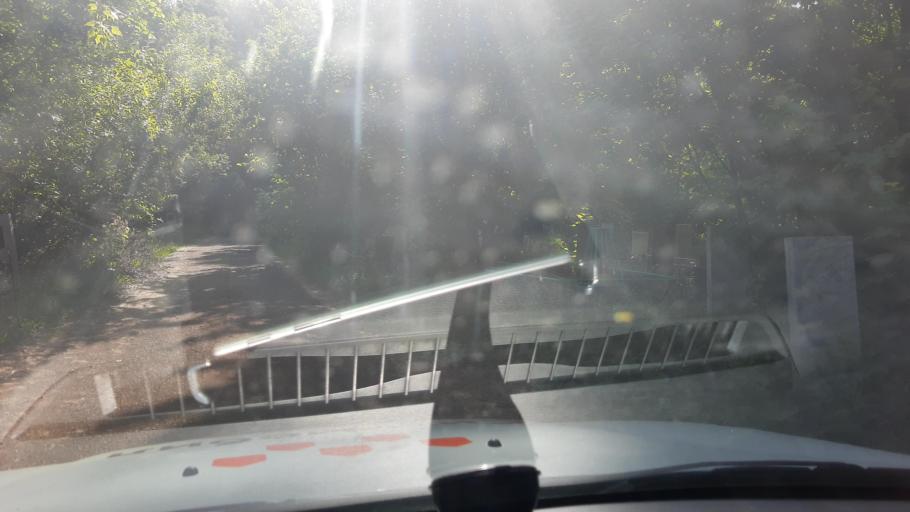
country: RU
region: Bashkortostan
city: Mikhaylovka
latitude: 54.8092
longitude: 55.8696
